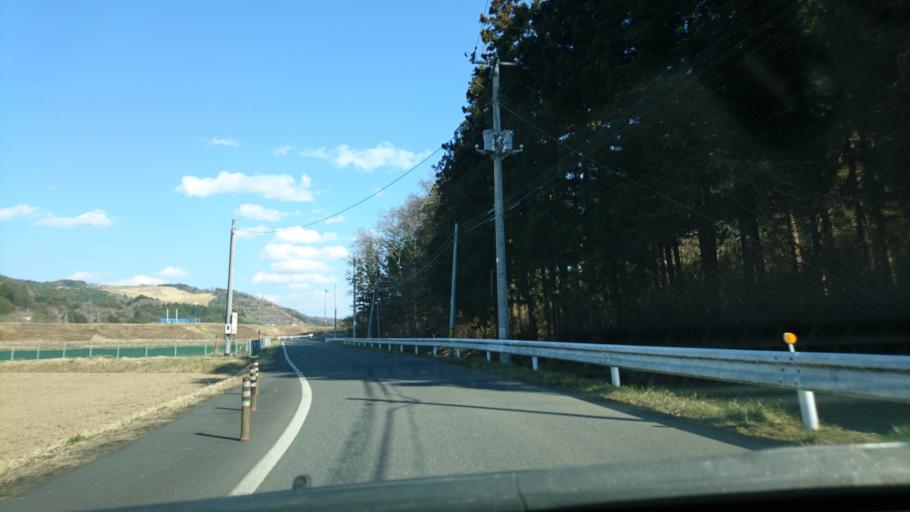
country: JP
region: Iwate
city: Ichinoseki
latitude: 38.8091
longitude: 141.2100
